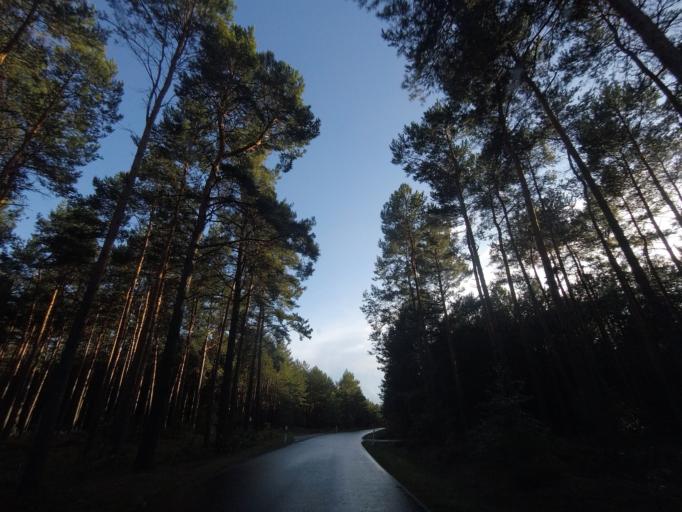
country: DE
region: Brandenburg
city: Treuenbrietzen
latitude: 52.0493
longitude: 12.8730
